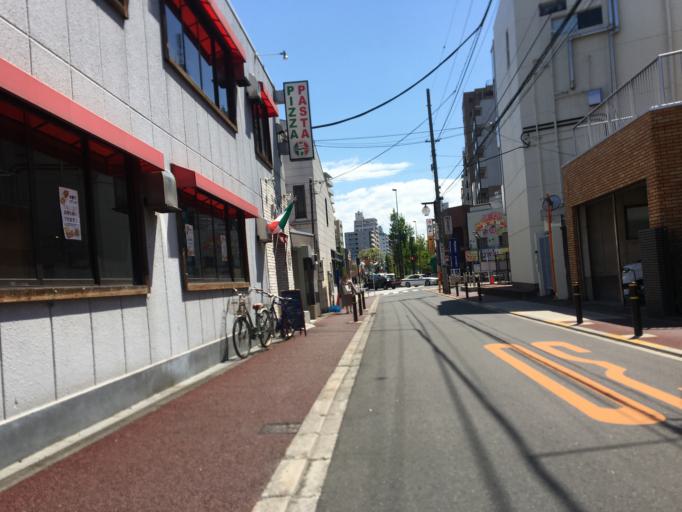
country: JP
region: Saitama
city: Kawaguchi
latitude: 35.7767
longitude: 139.6941
